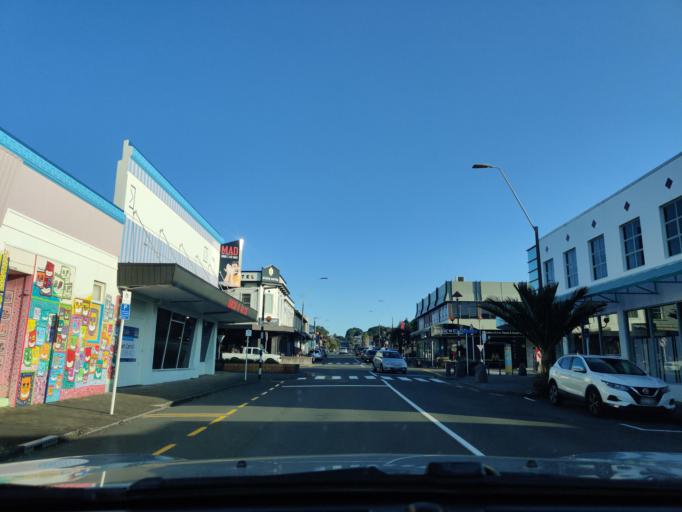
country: NZ
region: Taranaki
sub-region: New Plymouth District
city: New Plymouth
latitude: -39.0559
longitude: 174.0789
